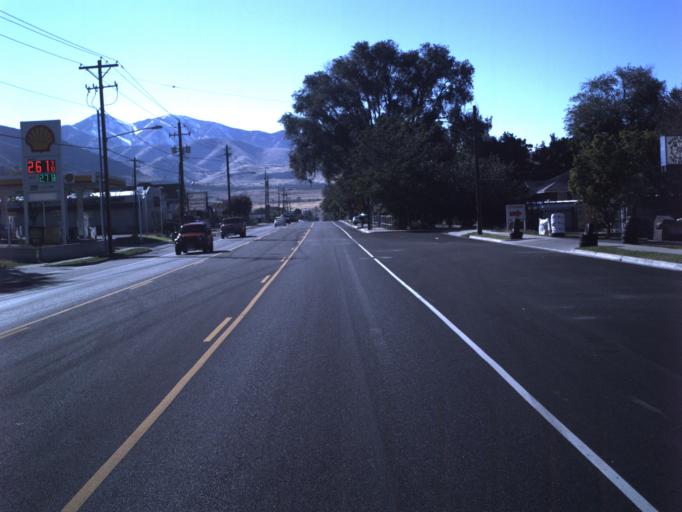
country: US
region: Utah
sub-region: Salt Lake County
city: Magna
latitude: 40.6965
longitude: -112.0846
